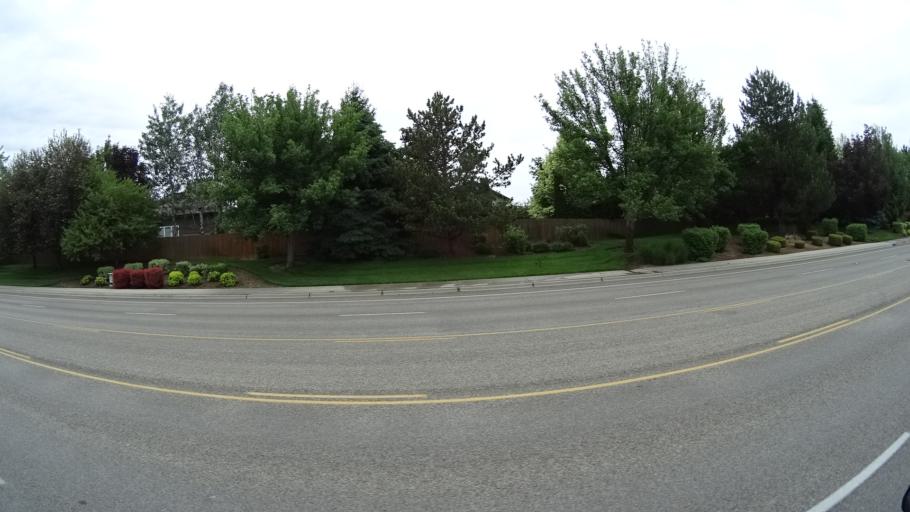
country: US
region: Idaho
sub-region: Ada County
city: Eagle
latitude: 43.6483
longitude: -116.3493
